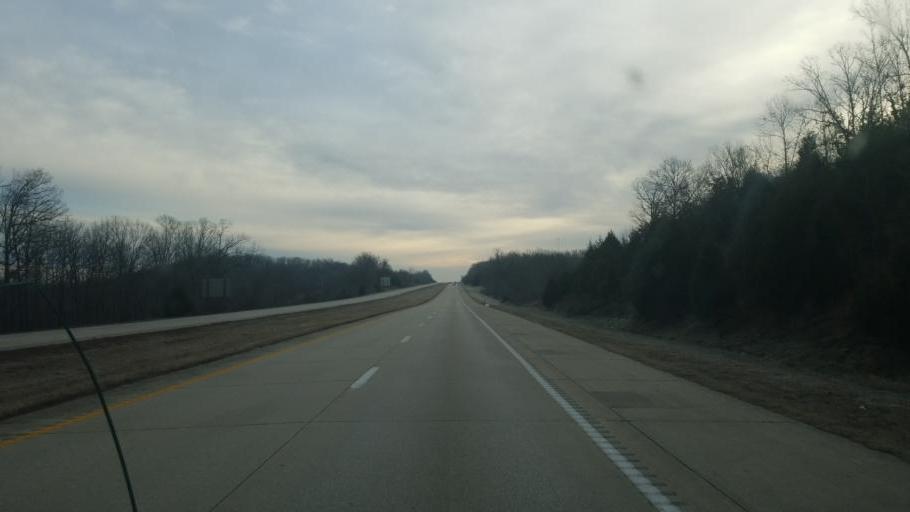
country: US
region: Missouri
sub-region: Butler County
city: Poplar Bluff
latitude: 36.7954
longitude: -90.4240
